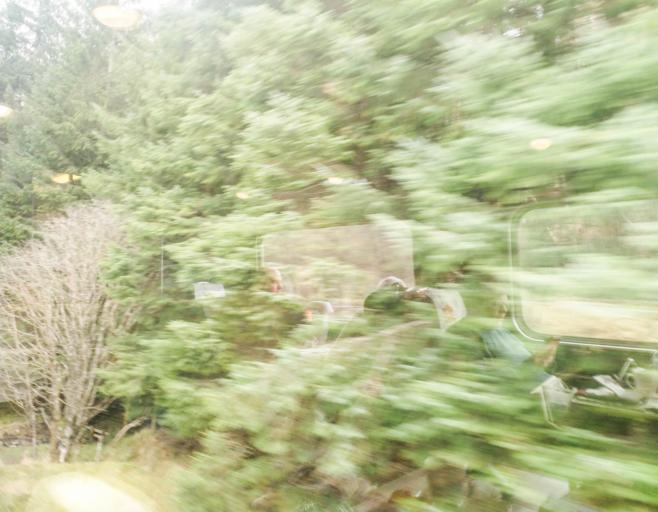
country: GB
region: Scotland
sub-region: Argyll and Bute
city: Garelochhead
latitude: 56.4444
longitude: -4.7079
